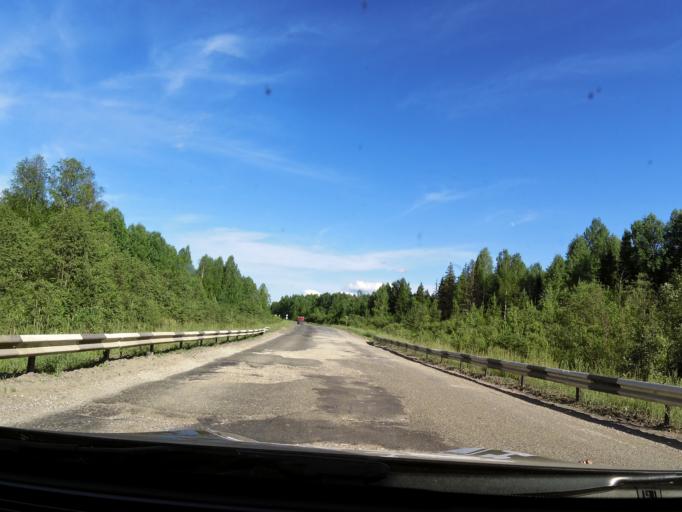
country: RU
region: Kirov
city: Chernaya Kholunitsa
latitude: 58.8926
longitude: 51.3382
